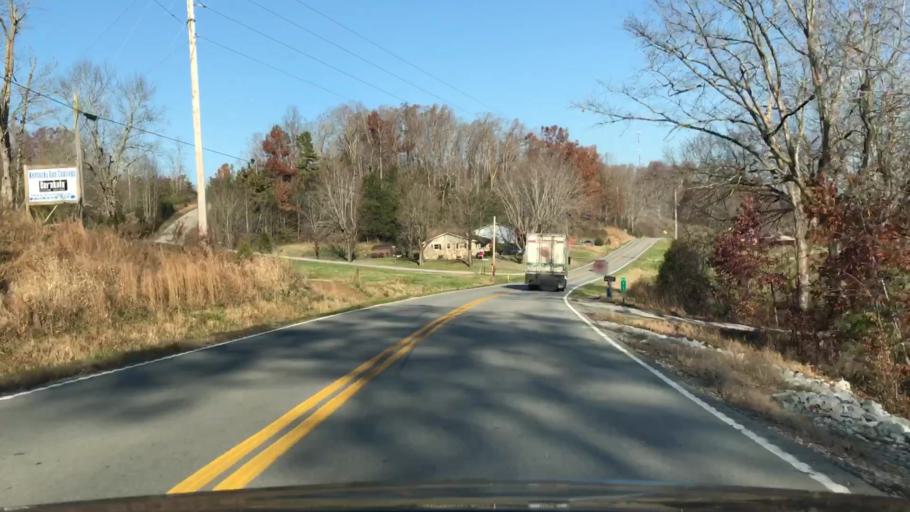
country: US
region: Kentucky
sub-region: Grayson County
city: Leitchfield
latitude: 37.4467
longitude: -86.2898
